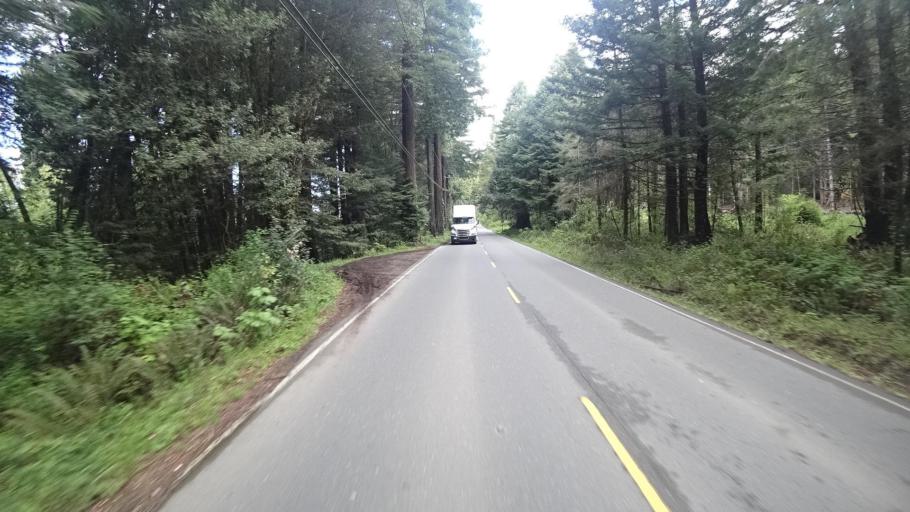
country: US
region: California
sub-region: Humboldt County
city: Blue Lake
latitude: 40.8708
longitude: -123.9742
